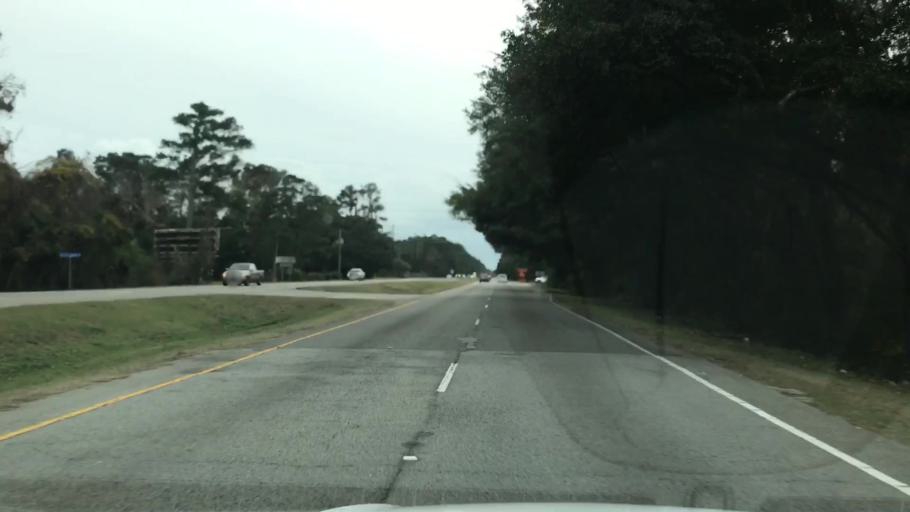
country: US
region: South Carolina
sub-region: Georgetown County
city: Murrells Inlet
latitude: 33.5250
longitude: -79.0654
